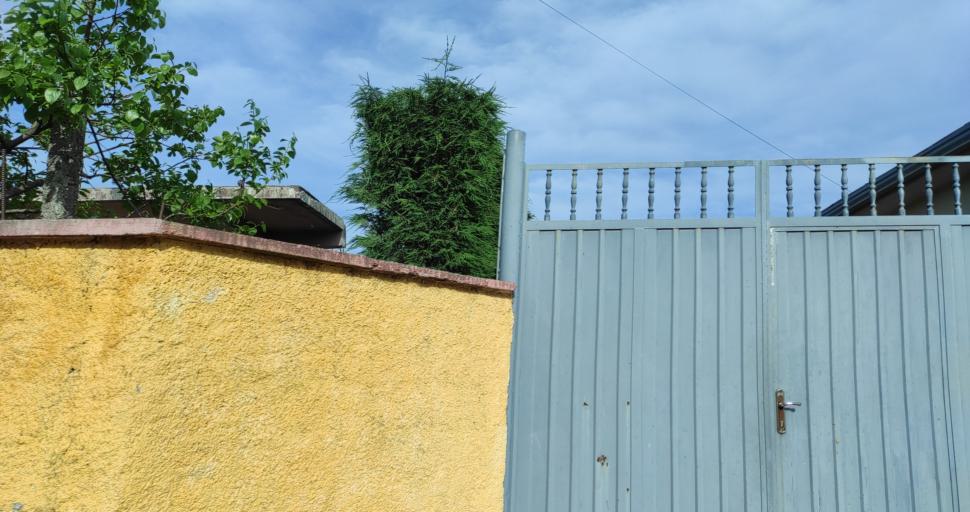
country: AL
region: Shkoder
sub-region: Rrethi i Shkodres
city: Shkoder
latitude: 42.0598
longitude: 19.5278
